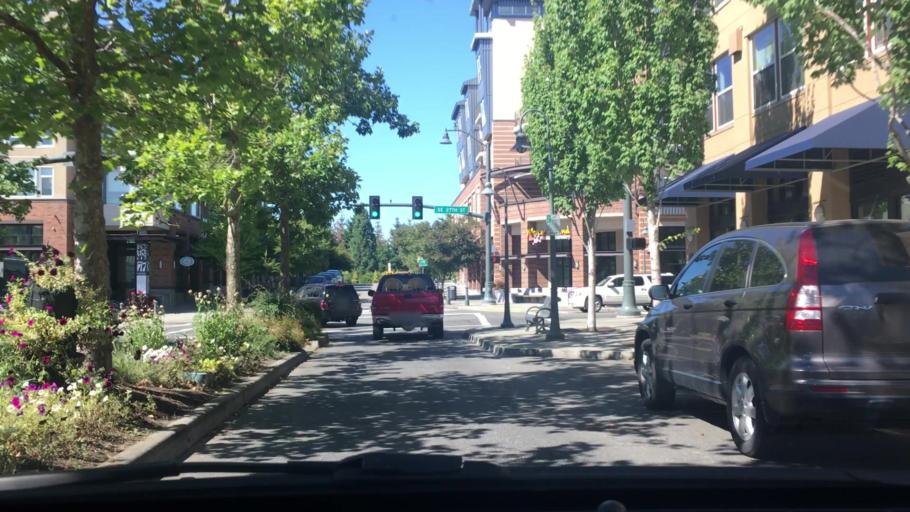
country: US
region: Washington
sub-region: King County
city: Mercer Island
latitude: 47.5863
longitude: -122.2336
